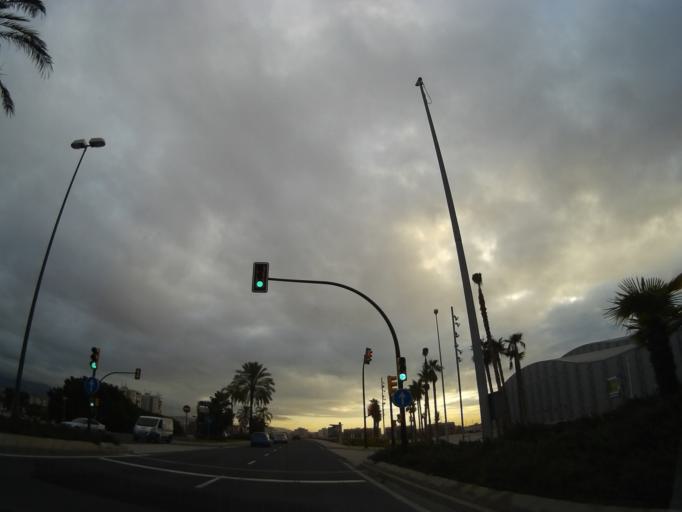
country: ES
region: Andalusia
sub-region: Provincia de Malaga
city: Malaga
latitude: 36.7074
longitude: -4.4607
